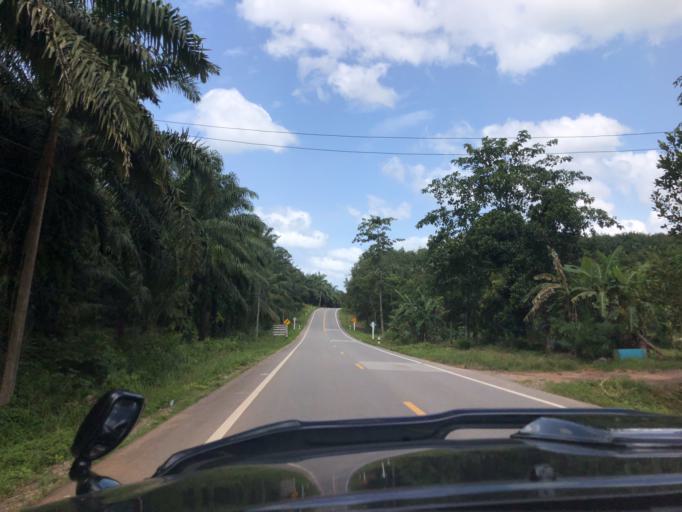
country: TH
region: Krabi
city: Khlong Thom
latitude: 7.9482
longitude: 99.2071
